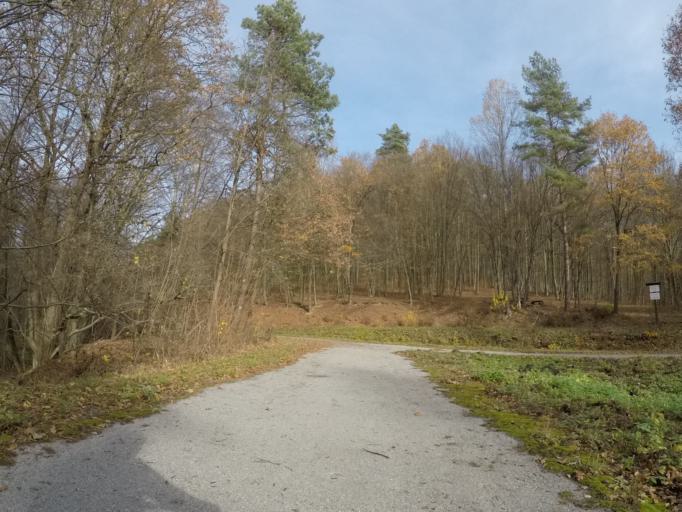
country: SK
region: Presovsky
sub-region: Okres Presov
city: Presov
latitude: 48.9592
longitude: 21.1939
